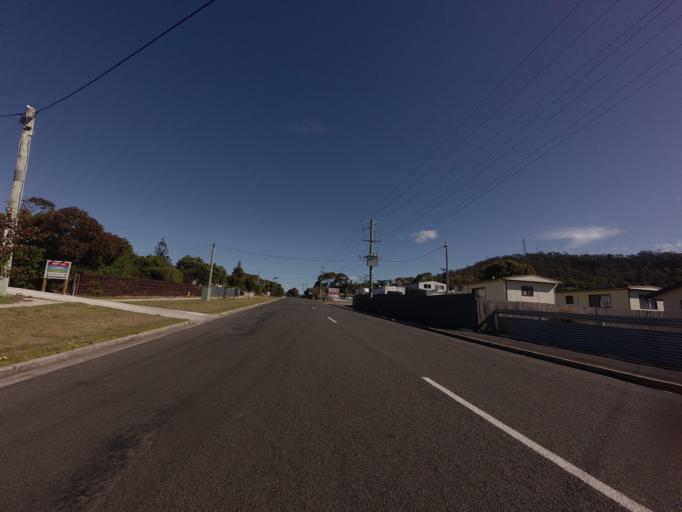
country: AU
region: Tasmania
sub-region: Break O'Day
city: St Helens
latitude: -41.8770
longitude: 148.3038
